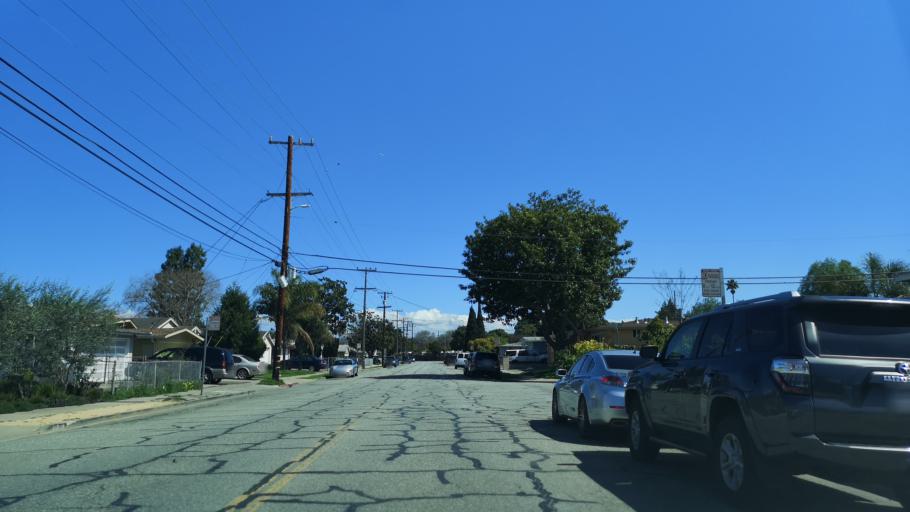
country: US
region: California
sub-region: San Mateo County
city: East Palo Alto
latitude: 37.4754
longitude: -122.1423
